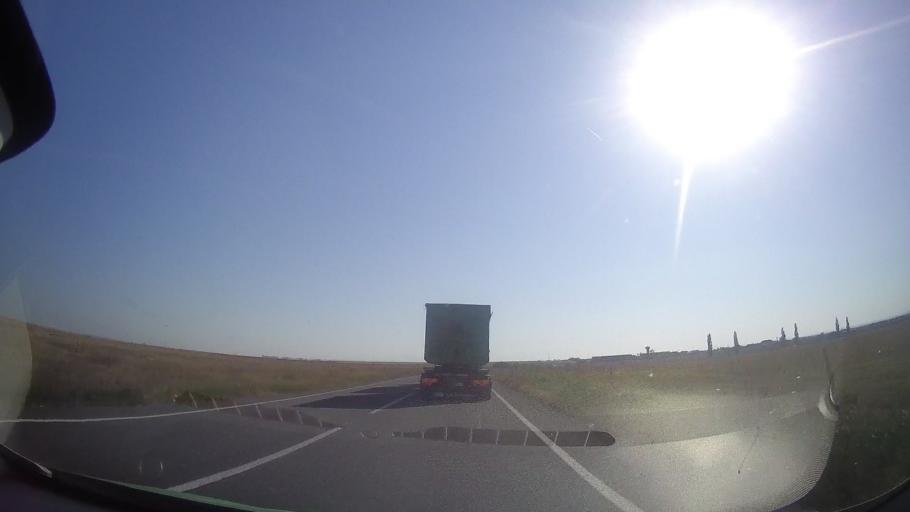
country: RO
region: Timis
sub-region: Comuna Ghizela
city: Ghizela
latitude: 45.7757
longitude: 21.6952
